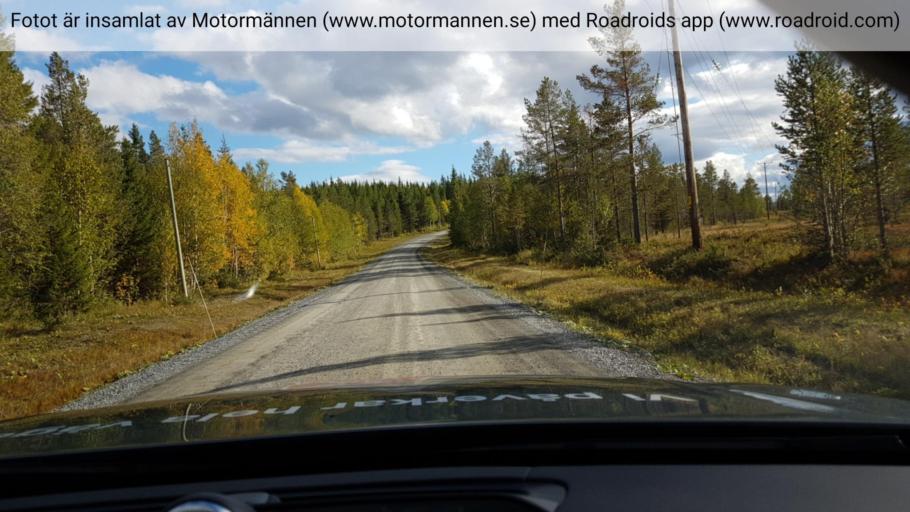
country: SE
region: Jaemtland
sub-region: Are Kommun
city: Jarpen
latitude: 63.2639
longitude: 13.6471
